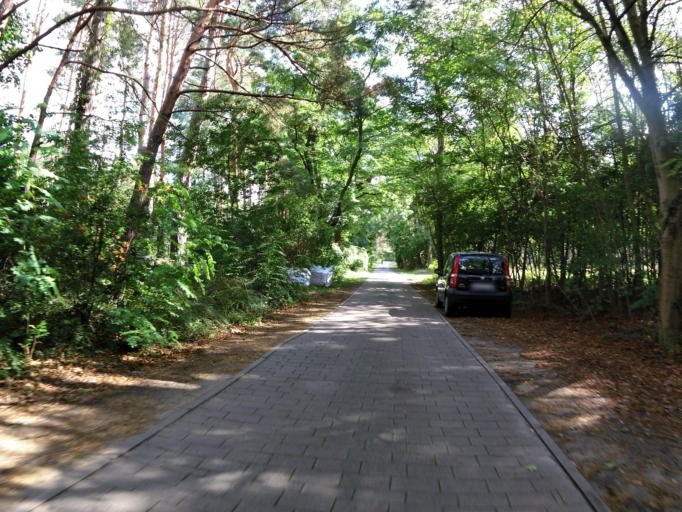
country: DE
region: Brandenburg
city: Munchehofe
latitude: 52.1897
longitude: 13.8805
